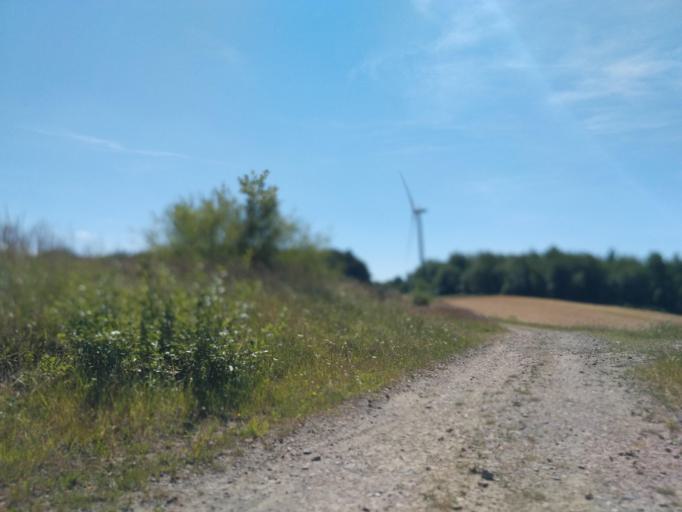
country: PL
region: Subcarpathian Voivodeship
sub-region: Powiat sanocki
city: Bukowsko
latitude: 49.5094
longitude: 22.0555
